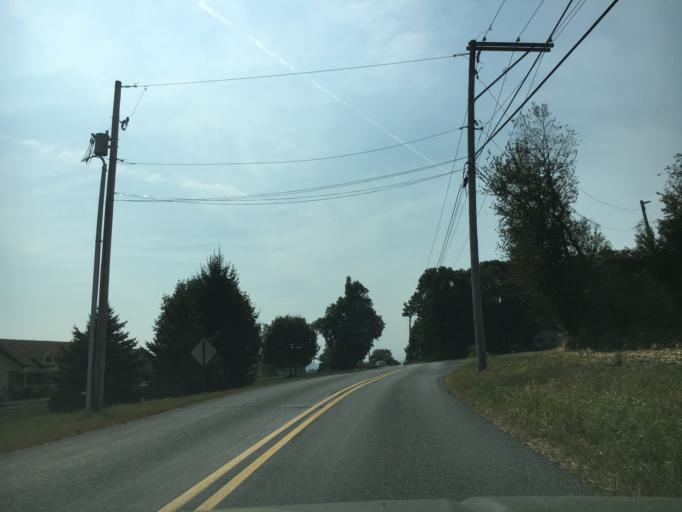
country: US
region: Pennsylvania
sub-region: Berks County
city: Topton
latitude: 40.5644
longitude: -75.7059
